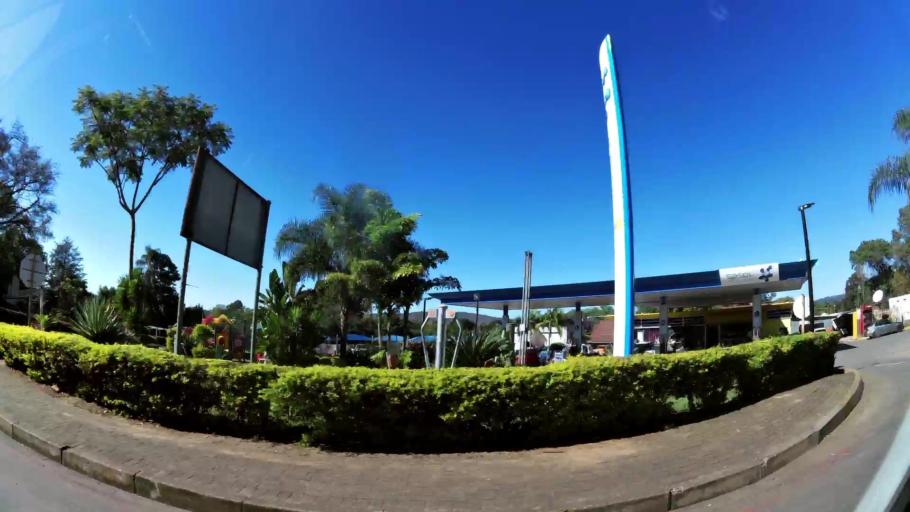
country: ZA
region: Limpopo
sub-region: Mopani District Municipality
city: Tzaneen
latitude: -23.8381
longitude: 30.1534
